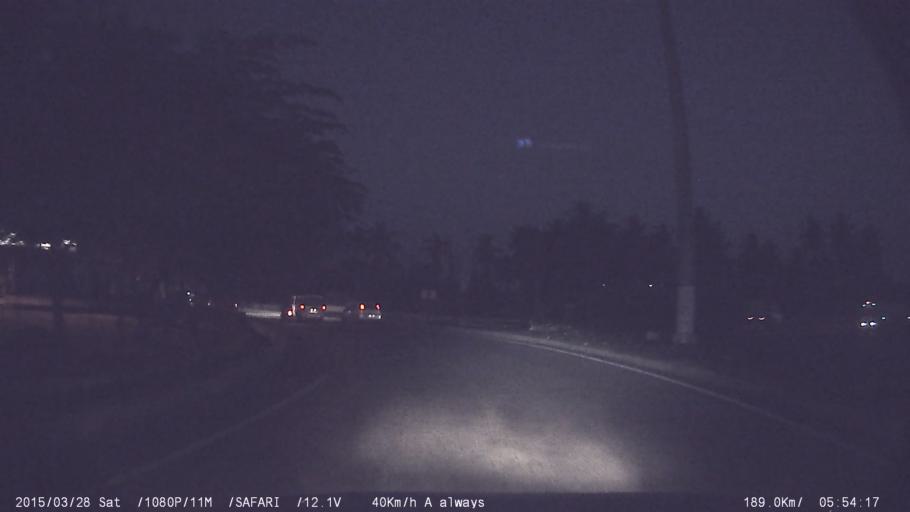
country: IN
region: Karnataka
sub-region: Bangalore Urban
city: Bangalore
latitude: 12.9022
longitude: 77.4701
